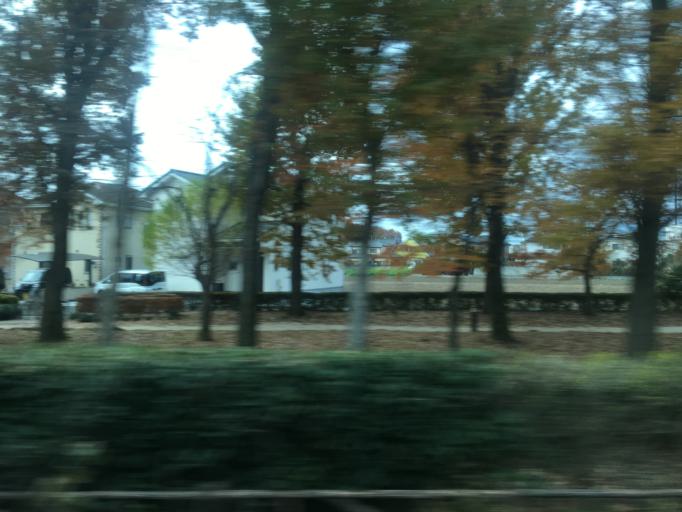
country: JP
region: Saitama
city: Okegawa
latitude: 36.0242
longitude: 139.5394
